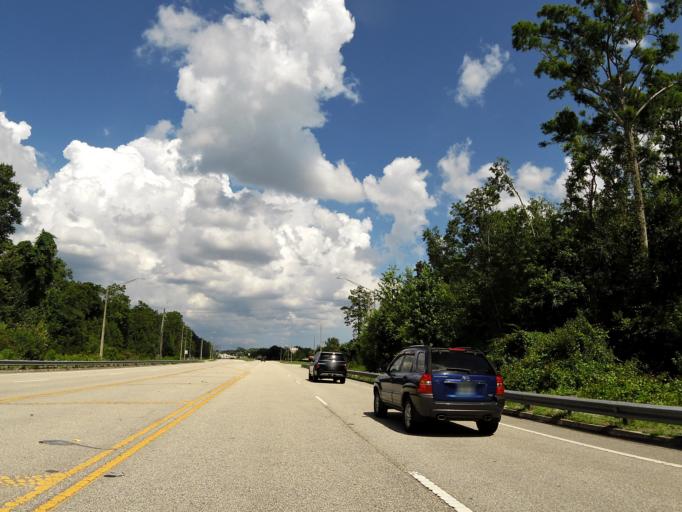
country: US
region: Florida
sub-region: Saint Johns County
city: Fruit Cove
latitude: 30.1436
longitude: -81.5553
